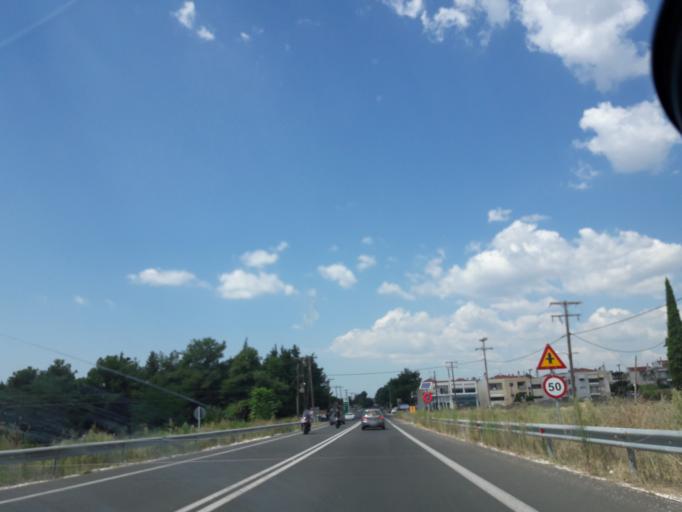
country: GR
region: Central Macedonia
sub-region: Nomos Thessalonikis
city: Agia Paraskevi
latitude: 40.5211
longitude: 23.0574
